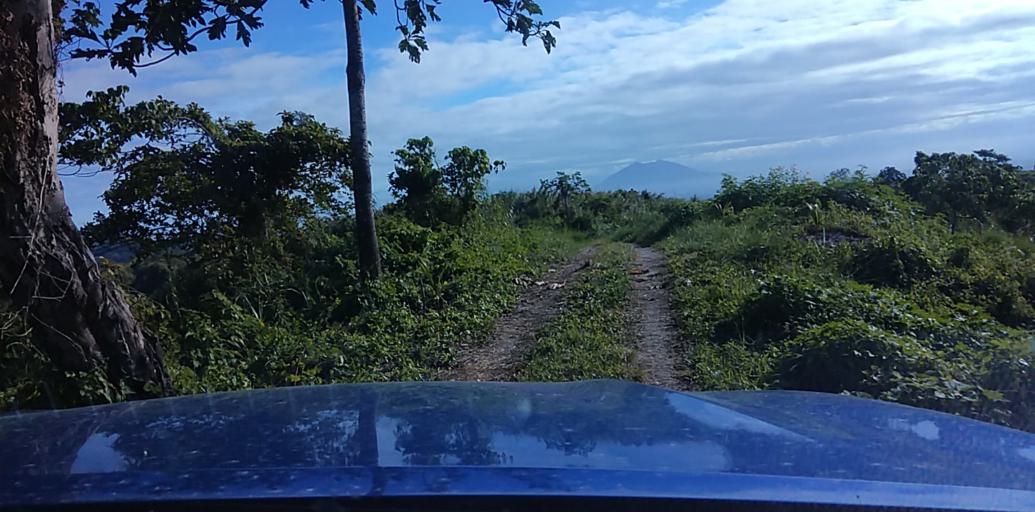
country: PH
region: Central Luzon
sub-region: Province of Pampanga
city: Babo-Pangulo
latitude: 15.1491
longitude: 120.4282
